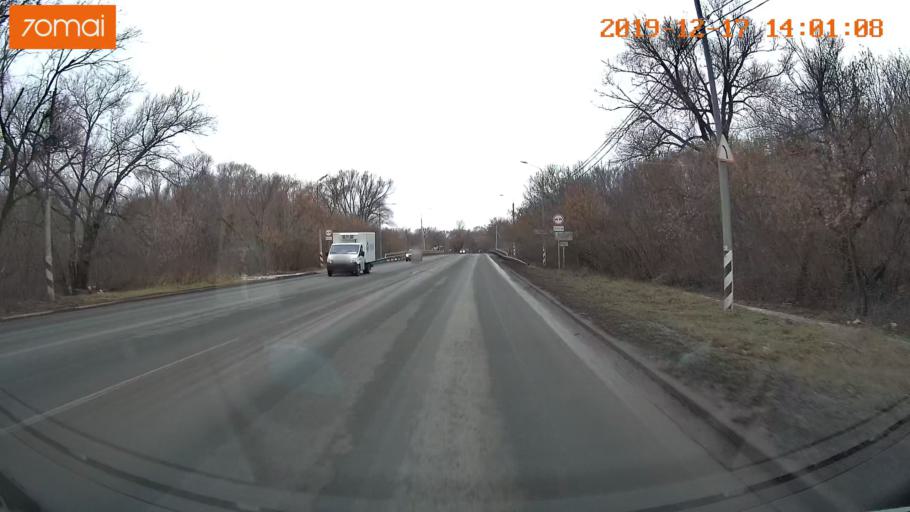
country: RU
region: Rjazan
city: Ryazan'
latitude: 54.6185
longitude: 39.6625
